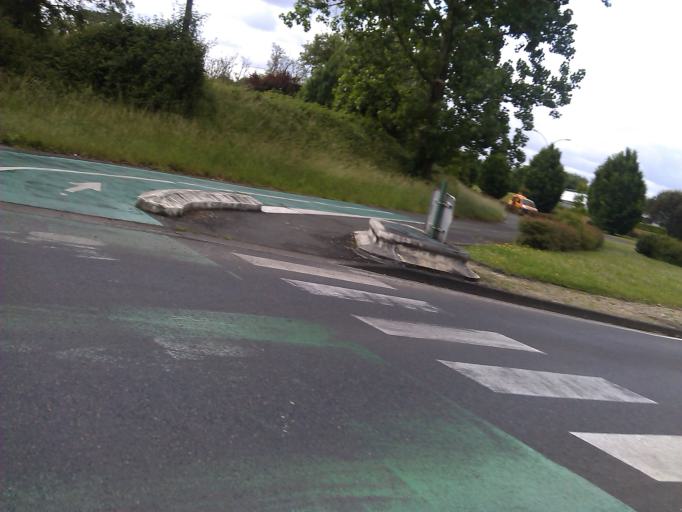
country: FR
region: Aquitaine
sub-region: Departement de la Gironde
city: Cestas
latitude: 44.7555
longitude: -0.6853
